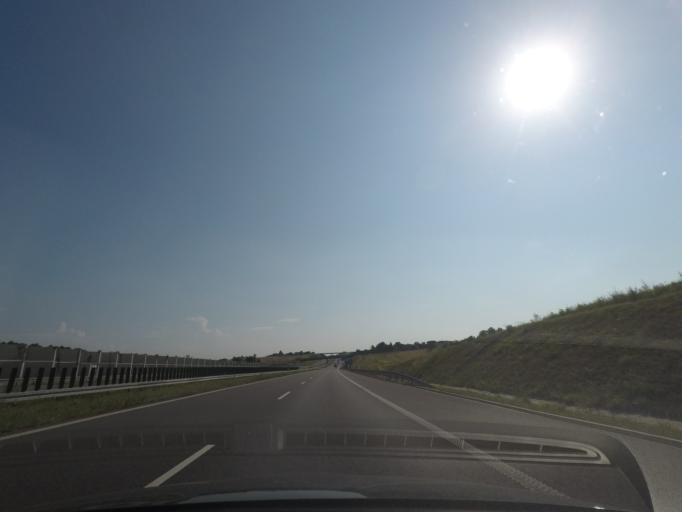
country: PL
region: Silesian Voivodeship
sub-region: Powiat rybnicki
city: Swierklany Dolne
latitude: 49.9985
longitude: 18.5754
